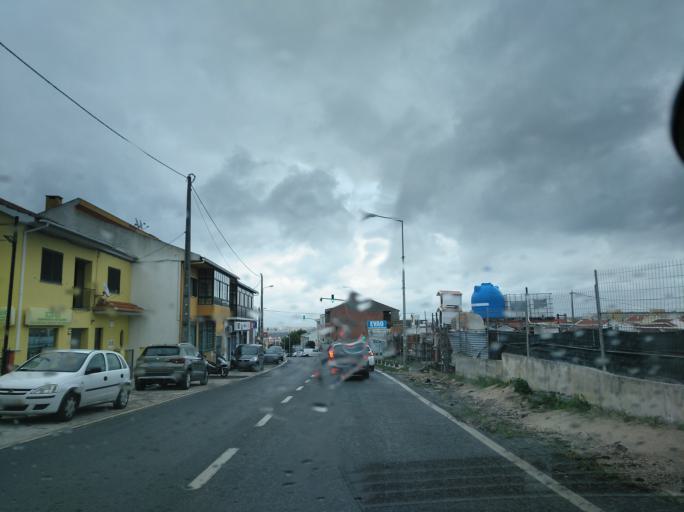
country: PT
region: Lisbon
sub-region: Odivelas
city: Famoes
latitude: 38.7864
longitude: -9.2245
